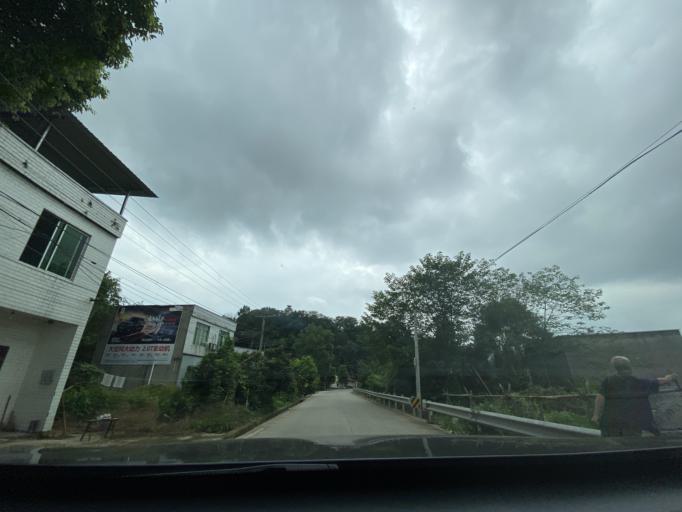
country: CN
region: Sichuan
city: Dongsheng
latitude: 30.4069
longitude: 104.0095
